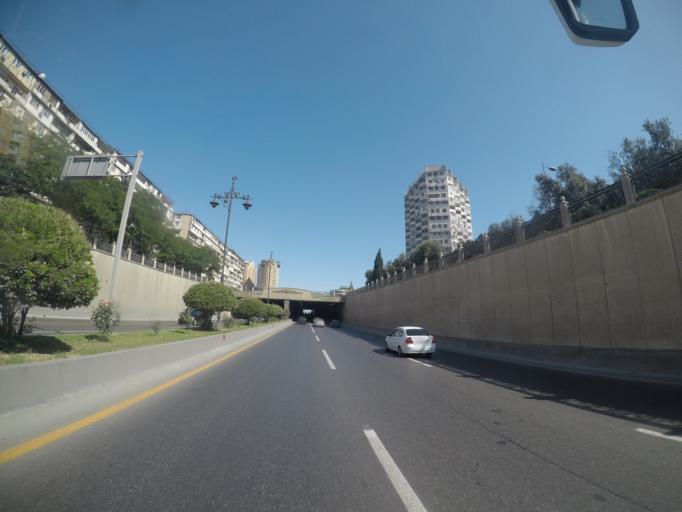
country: AZ
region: Baki
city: Bilajari
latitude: 40.4091
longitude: 49.8048
